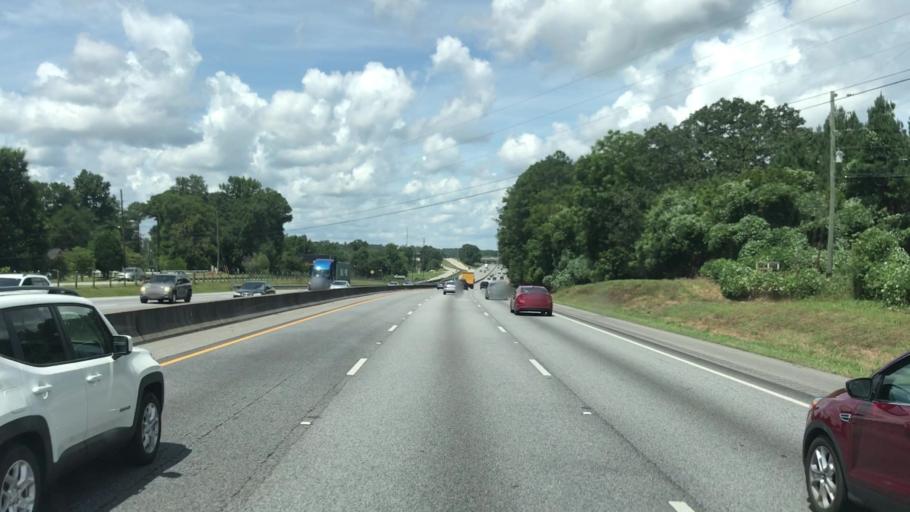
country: US
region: Georgia
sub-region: Newton County
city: Porterdale
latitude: 33.6144
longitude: -83.9099
